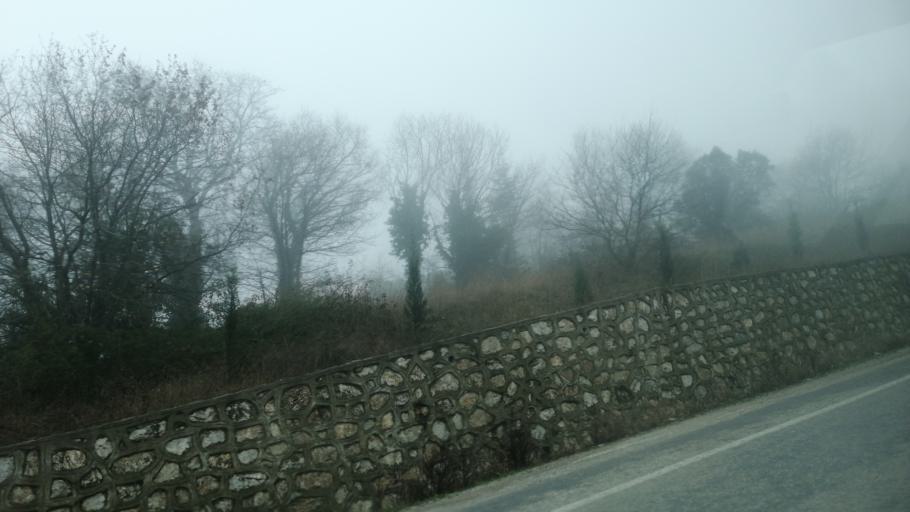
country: TR
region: Yalova
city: Korukoy
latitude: 40.6526
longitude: 29.1791
